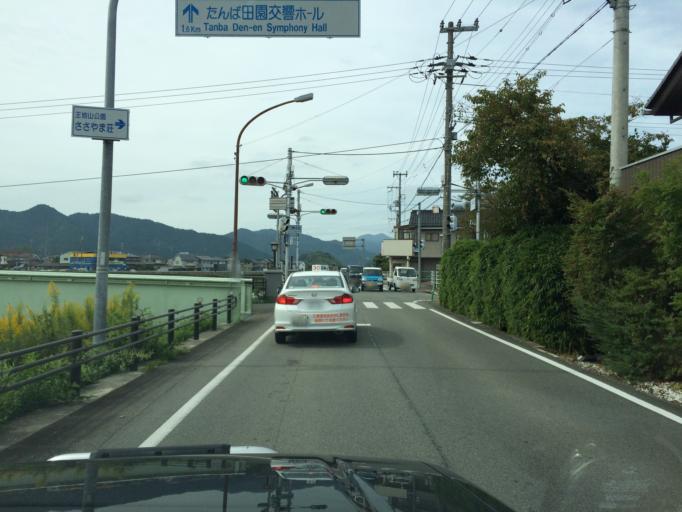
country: JP
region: Hyogo
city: Sasayama
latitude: 35.0713
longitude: 135.2292
